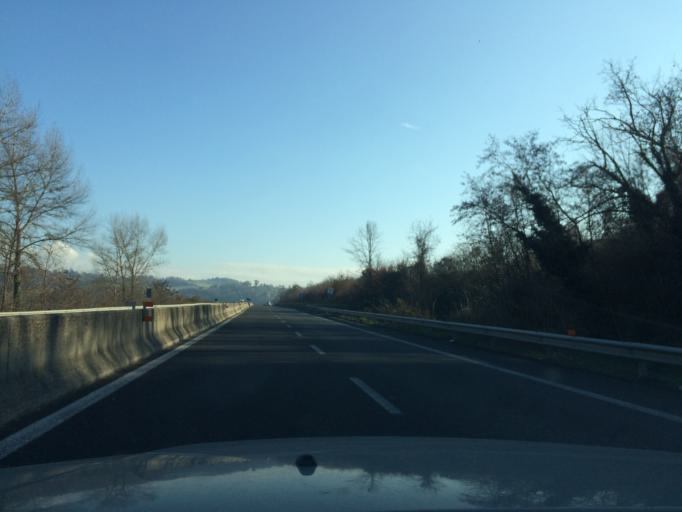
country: IT
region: Umbria
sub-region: Provincia di Perugia
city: Todi
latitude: 42.7820
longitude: 12.4377
